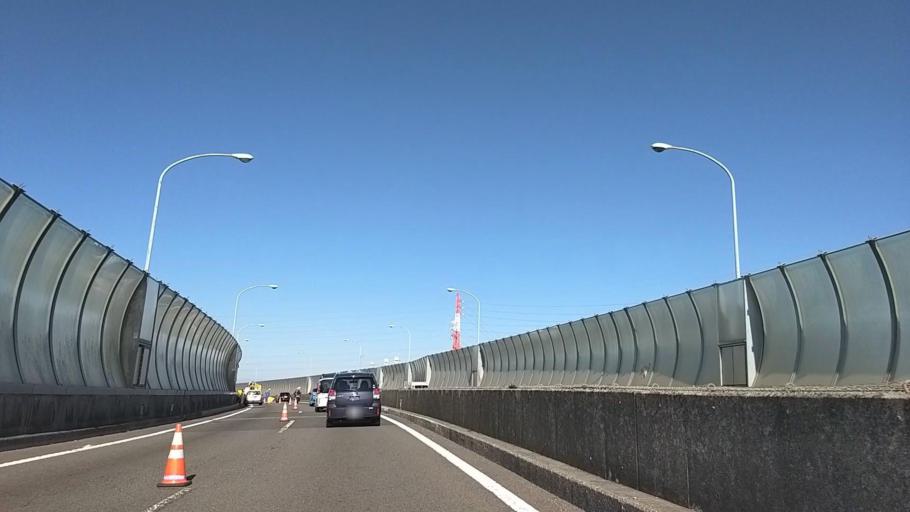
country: JP
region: Kanagawa
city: Minami-rinkan
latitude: 35.5013
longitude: 139.4909
